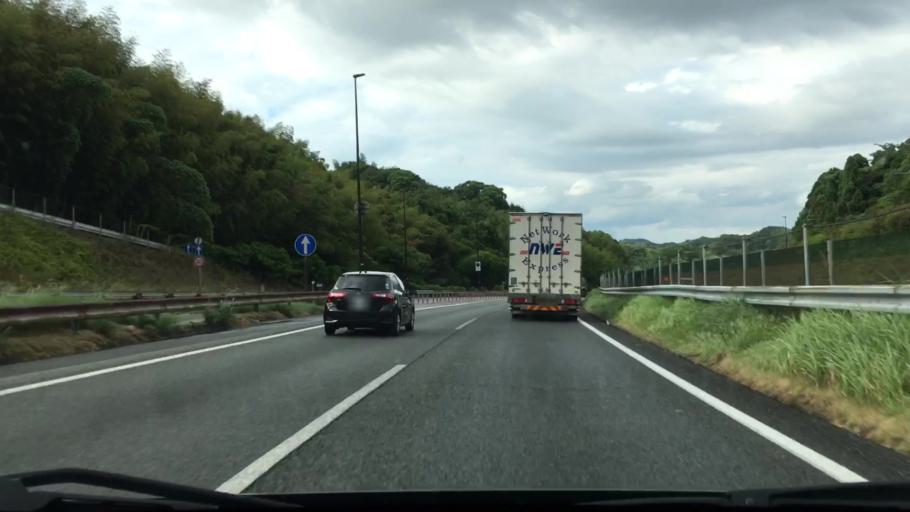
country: JP
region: Fukuoka
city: Nishifukuma
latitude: 33.7403
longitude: 130.5202
